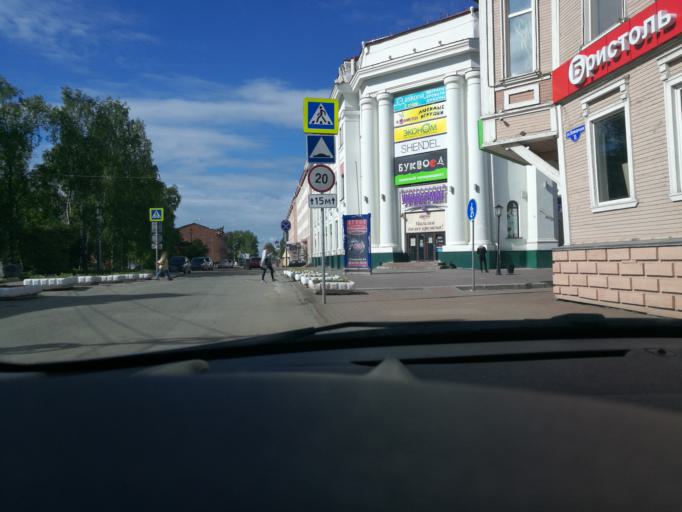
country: RU
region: Arkhangelskaya
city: Arkhangel'sk
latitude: 64.5361
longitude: 40.5269
